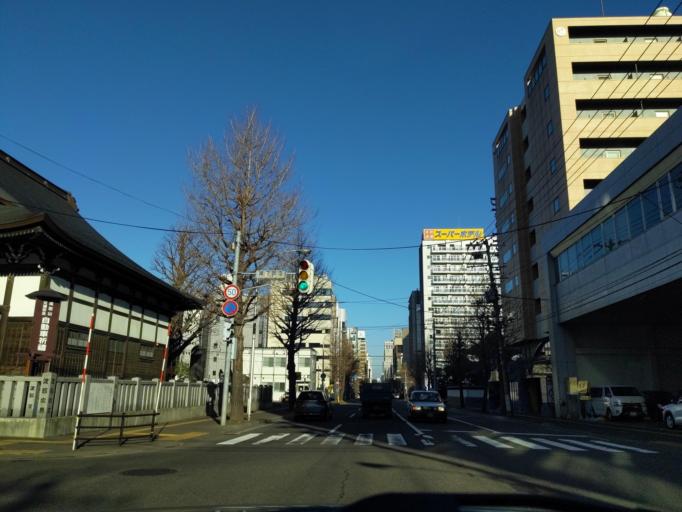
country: JP
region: Hokkaido
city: Sapporo
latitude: 43.0524
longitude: 141.3556
